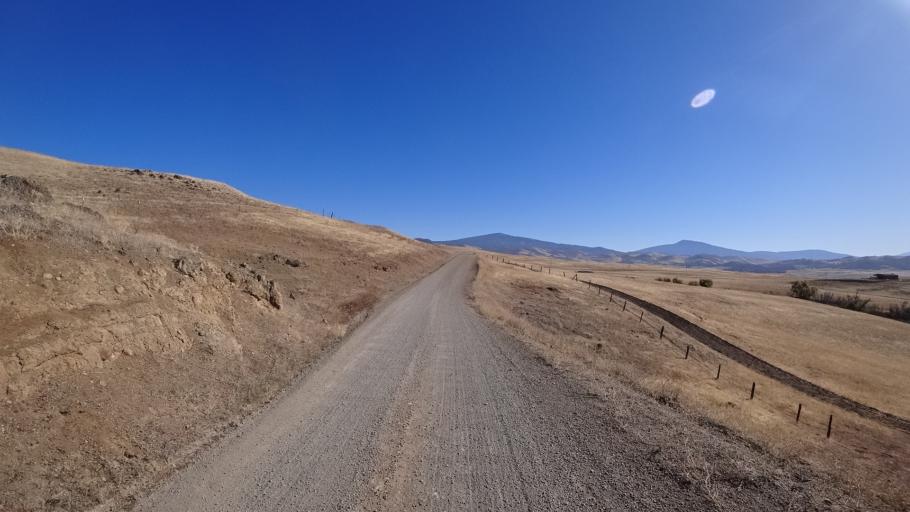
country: US
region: California
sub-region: Siskiyou County
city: Montague
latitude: 41.8441
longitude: -122.4260
